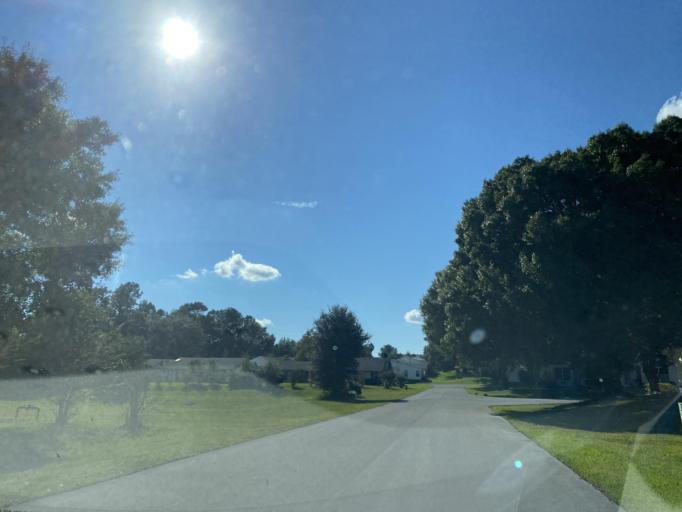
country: US
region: Florida
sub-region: Marion County
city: Ocala
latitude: 29.0531
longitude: -82.2540
